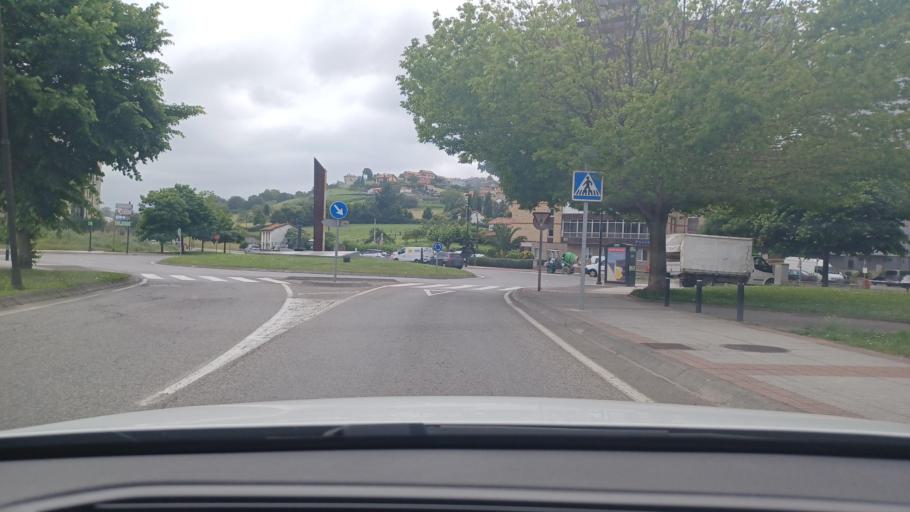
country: ES
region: Asturias
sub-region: Province of Asturias
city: Aviles
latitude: 43.5714
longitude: -5.9598
